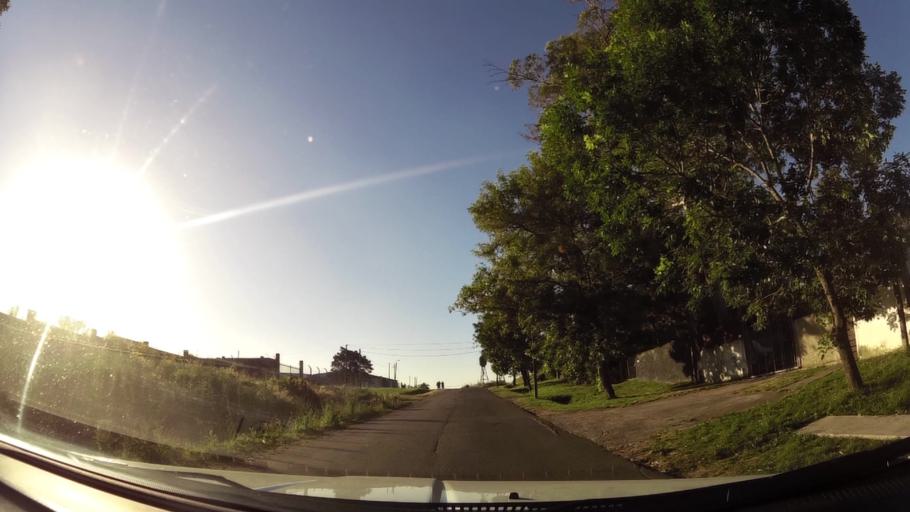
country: UY
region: Canelones
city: La Paz
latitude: -34.8300
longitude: -56.2442
